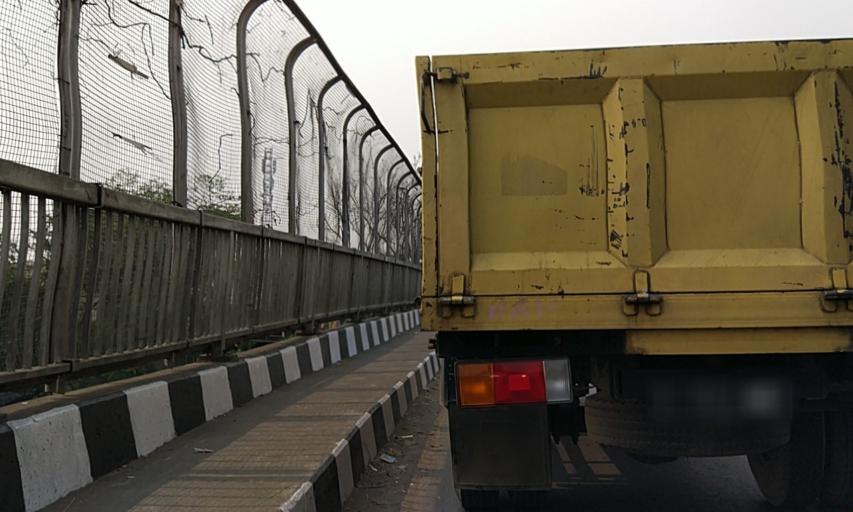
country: ID
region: West Java
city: Margahayukencana
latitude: -6.9522
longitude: 107.5641
